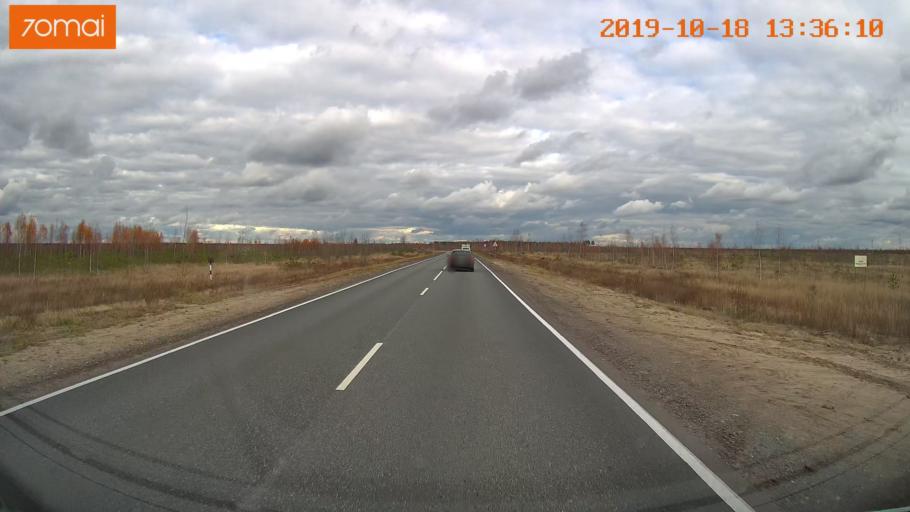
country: RU
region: Rjazan
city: Solotcha
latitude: 54.8675
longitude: 39.9817
